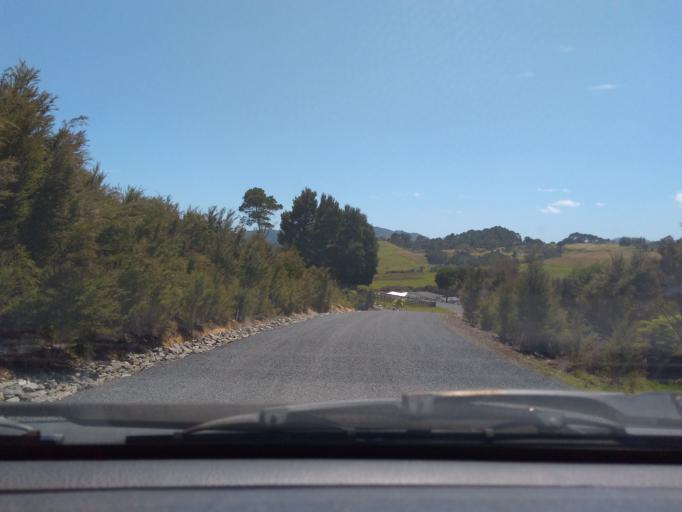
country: NZ
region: Northland
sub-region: Far North District
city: Taipa
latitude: -34.9979
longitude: 173.5109
